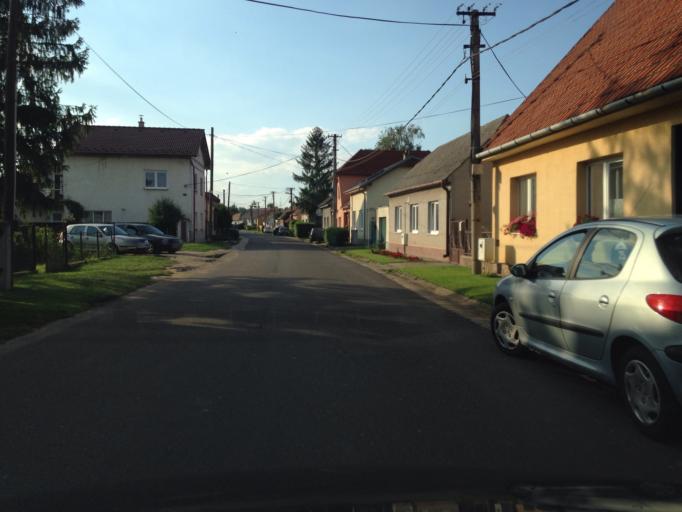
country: AT
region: Lower Austria
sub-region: Politischer Bezirk Ganserndorf
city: Angern an der March
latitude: 48.4044
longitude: 16.8599
